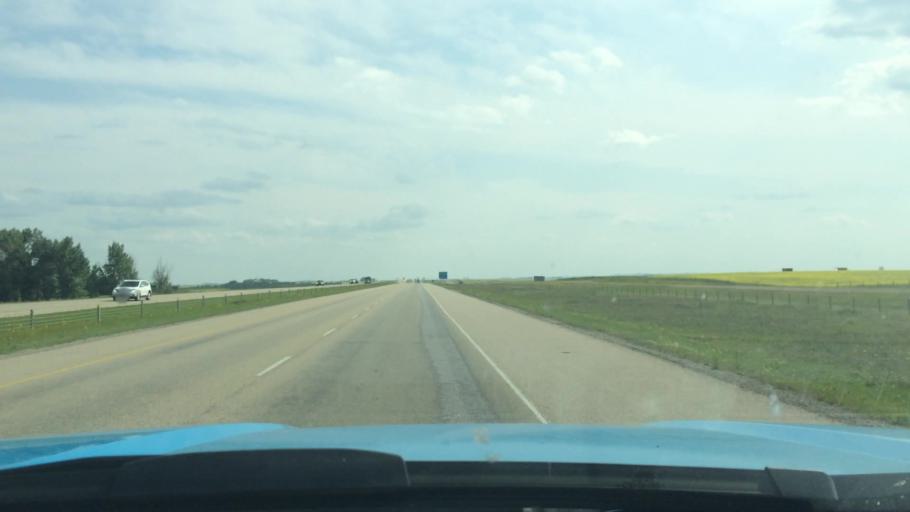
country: CA
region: Alberta
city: Carstairs
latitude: 51.5862
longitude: -114.0253
